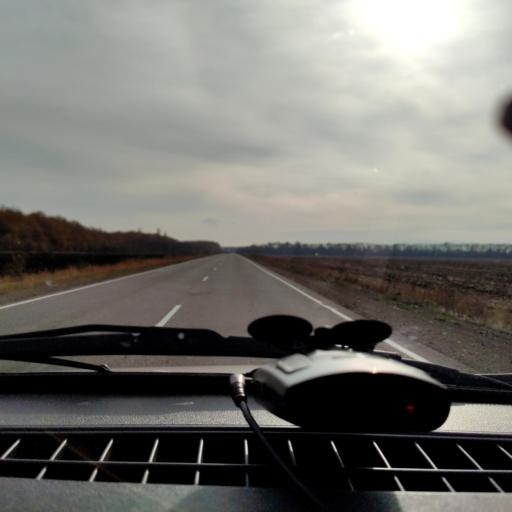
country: RU
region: Voronezj
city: Shilovo
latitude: 51.4385
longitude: 38.9990
